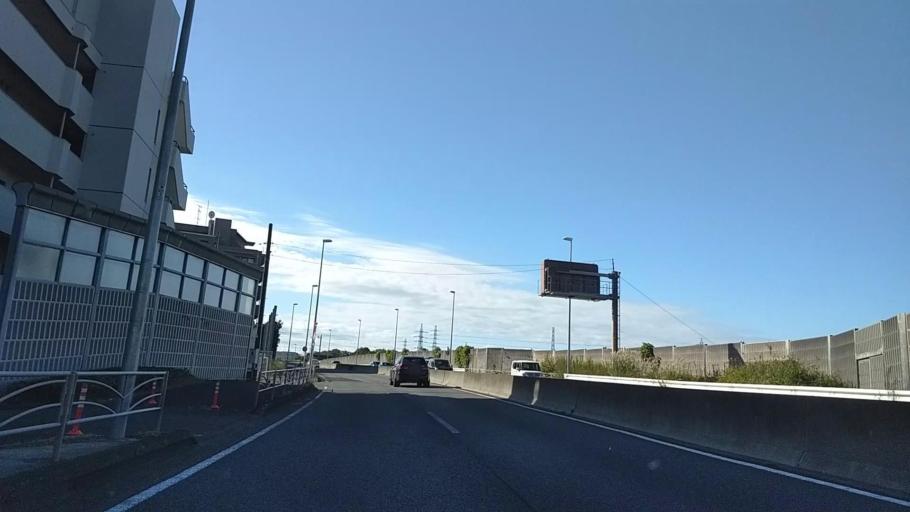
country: JP
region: Kanagawa
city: Fujisawa
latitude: 35.4068
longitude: 139.5289
